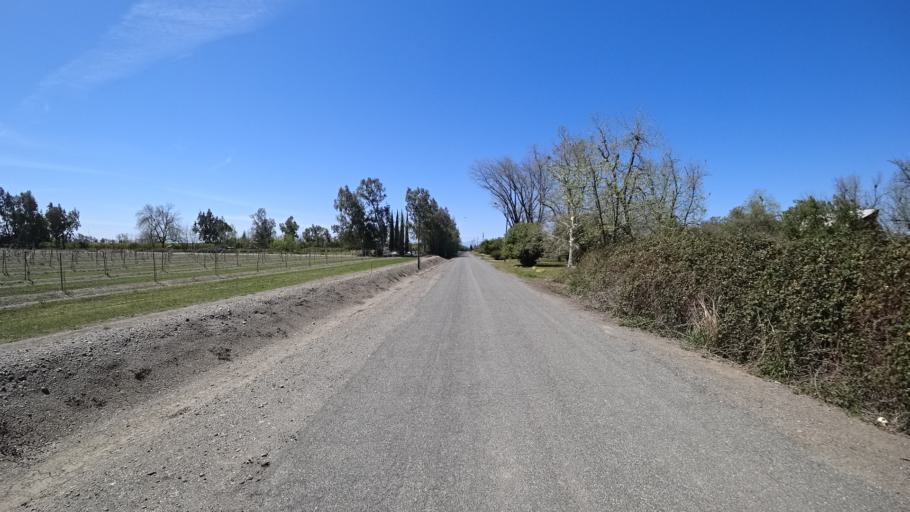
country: US
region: California
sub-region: Glenn County
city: Hamilton City
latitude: 39.7285
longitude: -122.1007
